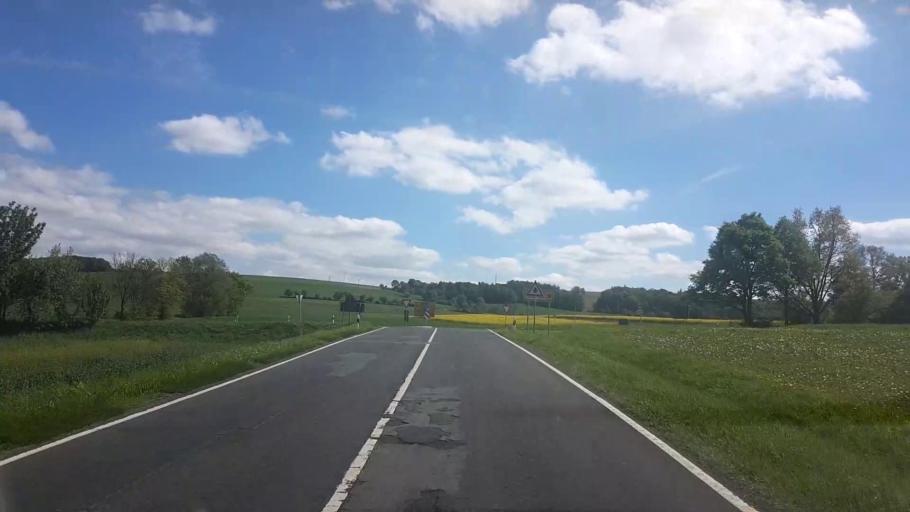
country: DE
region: Bavaria
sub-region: Regierungsbezirk Unterfranken
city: Untermerzbach
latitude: 50.1270
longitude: 10.8850
